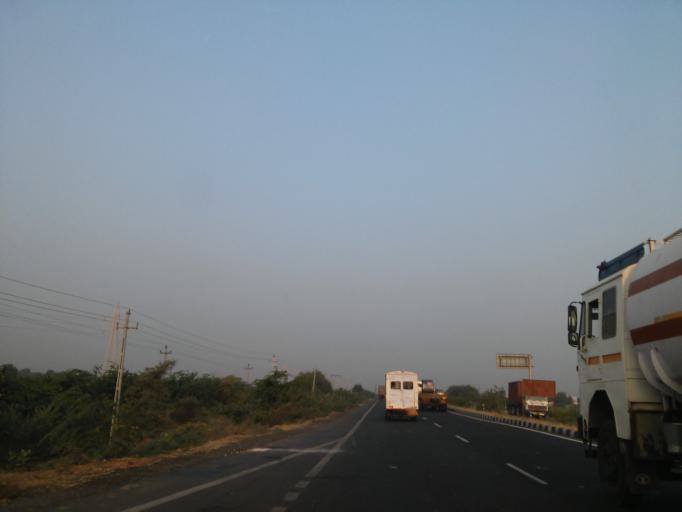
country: IN
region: Gujarat
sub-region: Kachchh
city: Bhachau
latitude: 23.2699
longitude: 70.6211
